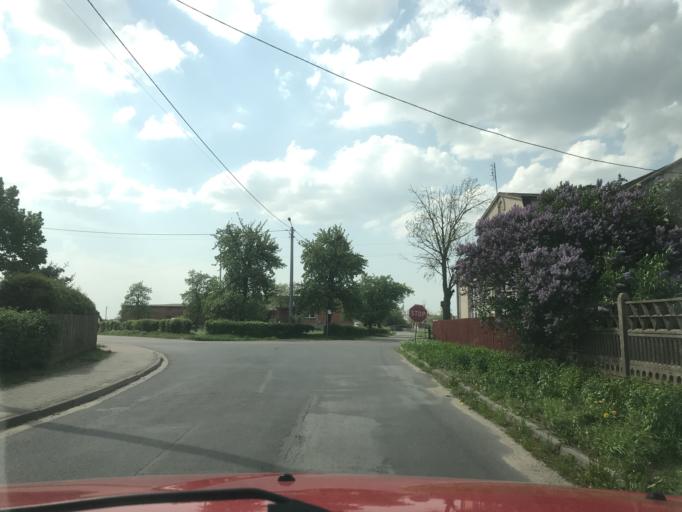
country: PL
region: Greater Poland Voivodeship
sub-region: Powiat kaliski
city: Zelazkow
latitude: 51.9538
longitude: 18.2414
